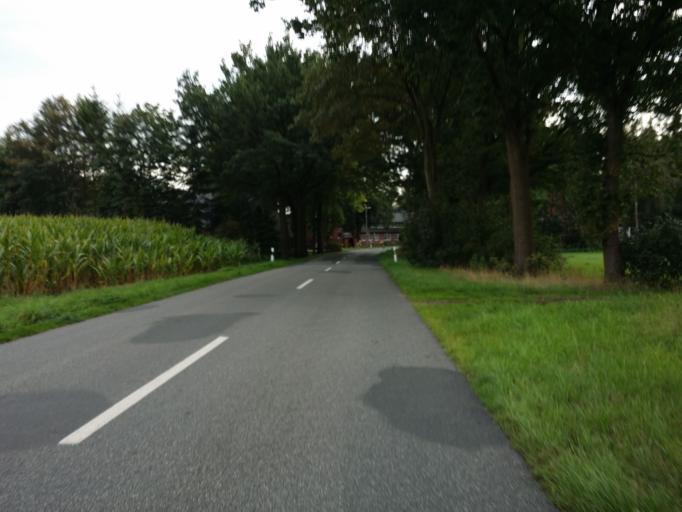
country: DE
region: Lower Saxony
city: Hollnseth
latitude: 53.5754
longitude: 9.1124
